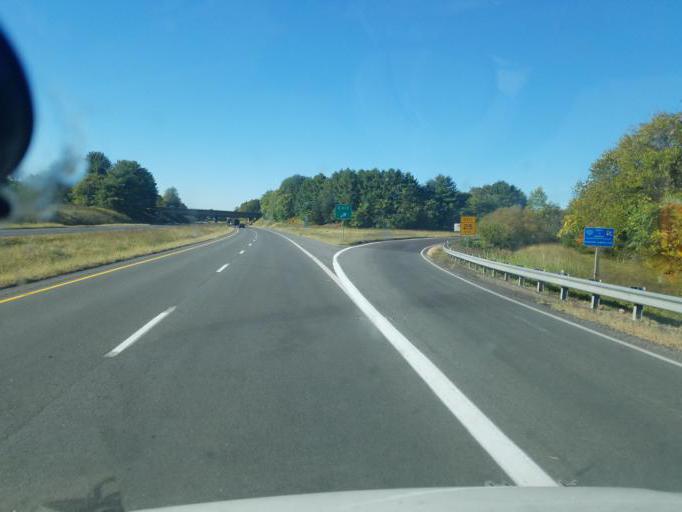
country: US
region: Virginia
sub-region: Culpeper County
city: Culpeper
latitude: 38.4919
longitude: -77.9356
